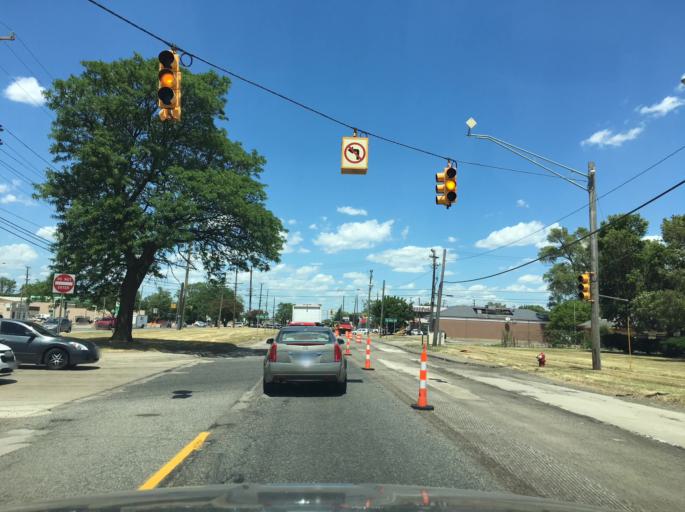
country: US
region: Michigan
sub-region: Macomb County
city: Warren
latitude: 42.4756
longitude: -83.0452
